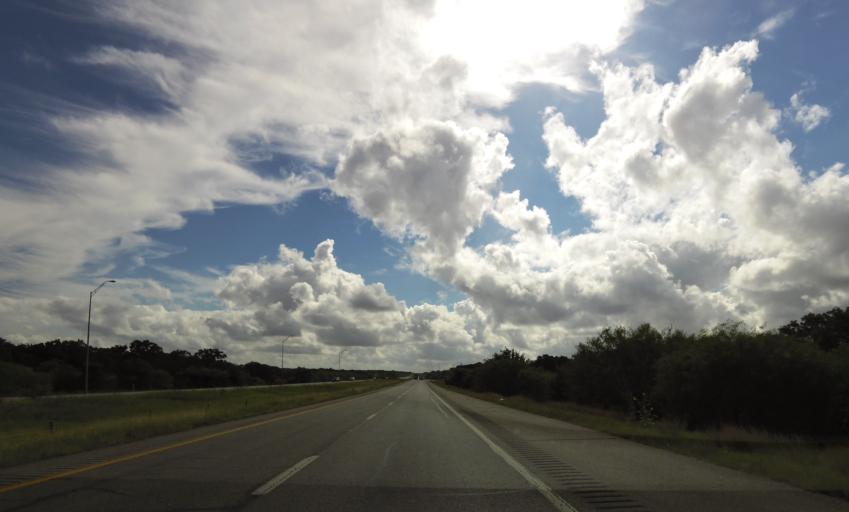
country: US
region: Texas
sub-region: Caldwell County
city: Luling
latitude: 29.6156
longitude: -97.8022
